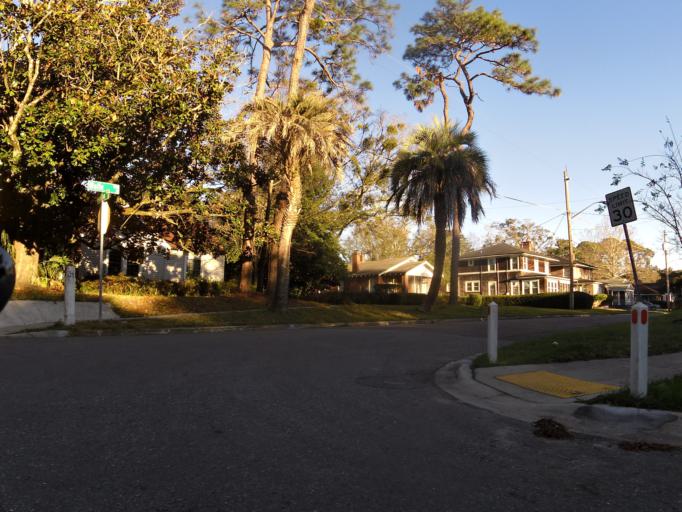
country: US
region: Florida
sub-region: Duval County
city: Jacksonville
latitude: 30.3112
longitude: -81.7221
